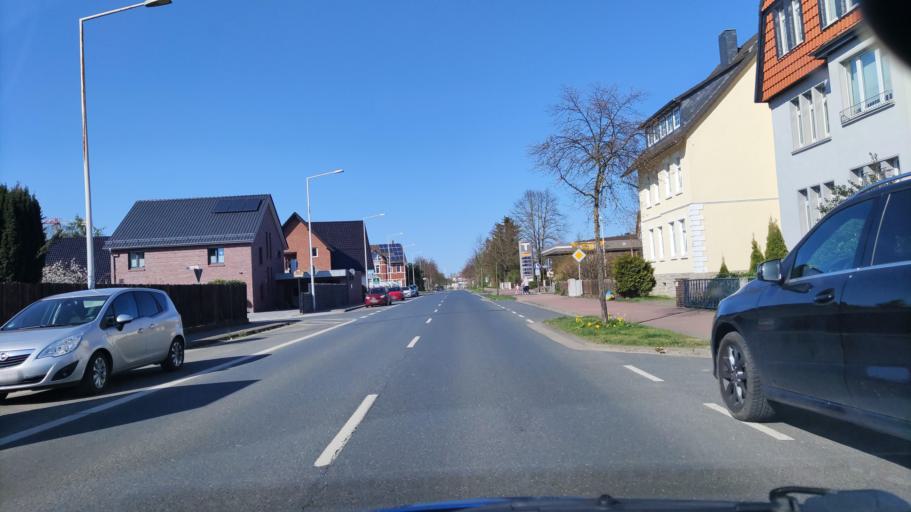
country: DE
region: Lower Saxony
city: Sehnde
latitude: 52.3173
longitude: 9.9651
